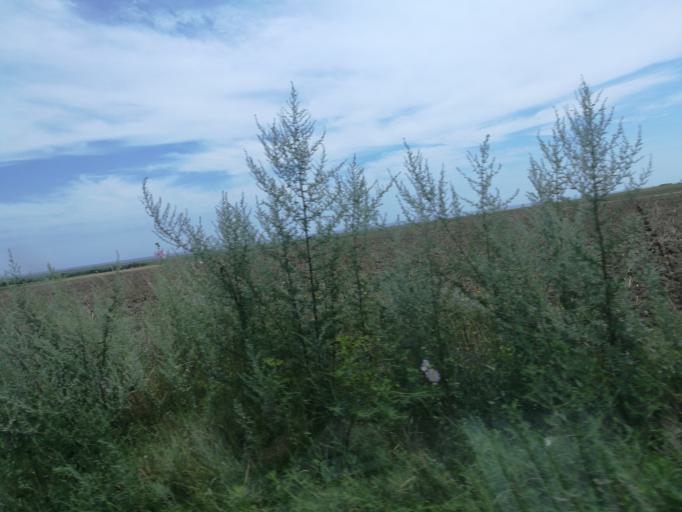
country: RO
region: Constanta
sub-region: Comuna Corbu
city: Corbu
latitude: 44.4279
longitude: 28.7148
